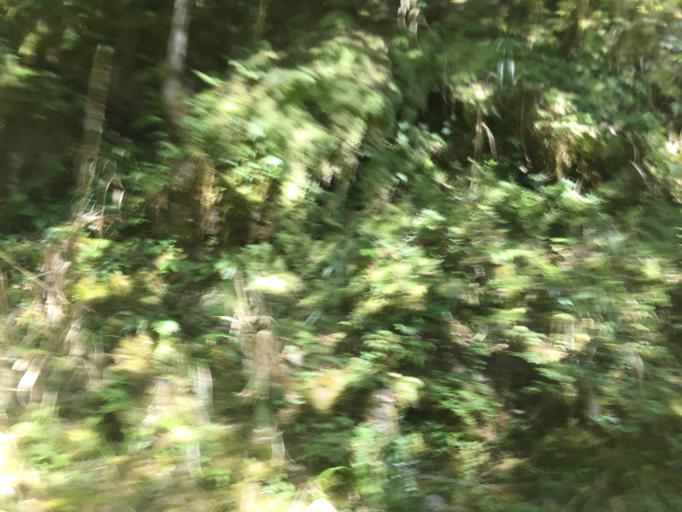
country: TW
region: Taiwan
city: Daxi
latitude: 24.5918
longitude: 121.4161
